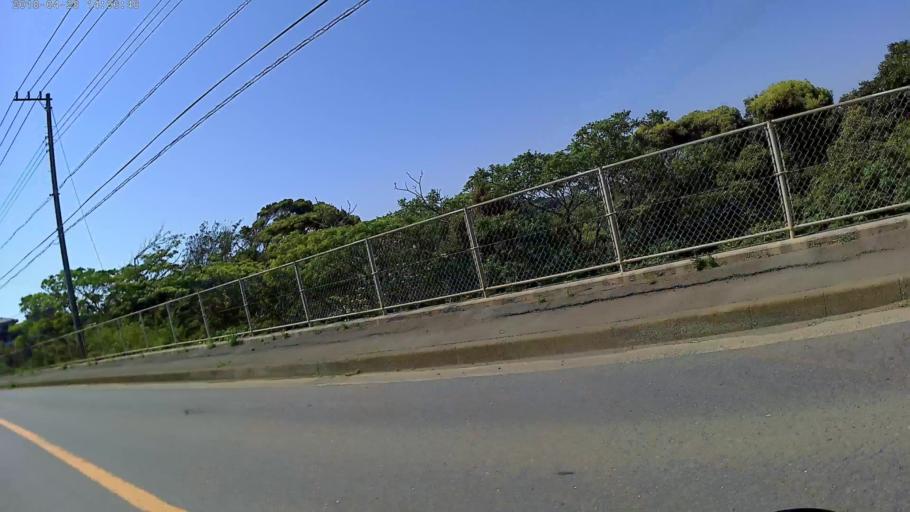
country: JP
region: Kanagawa
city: Miura
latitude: 35.1567
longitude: 139.6452
